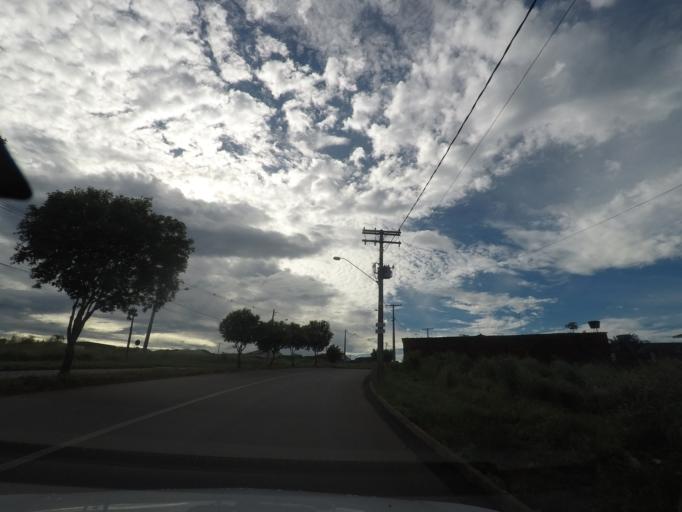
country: BR
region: Goias
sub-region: Aparecida De Goiania
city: Aparecida de Goiania
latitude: -16.7848
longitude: -49.3747
